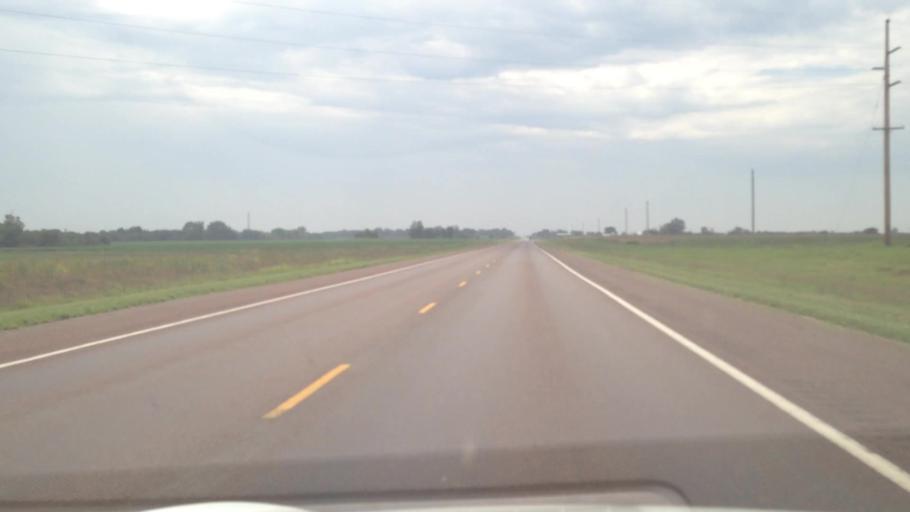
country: US
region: Kansas
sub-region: Crawford County
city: Girard
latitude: 37.4574
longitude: -94.8330
